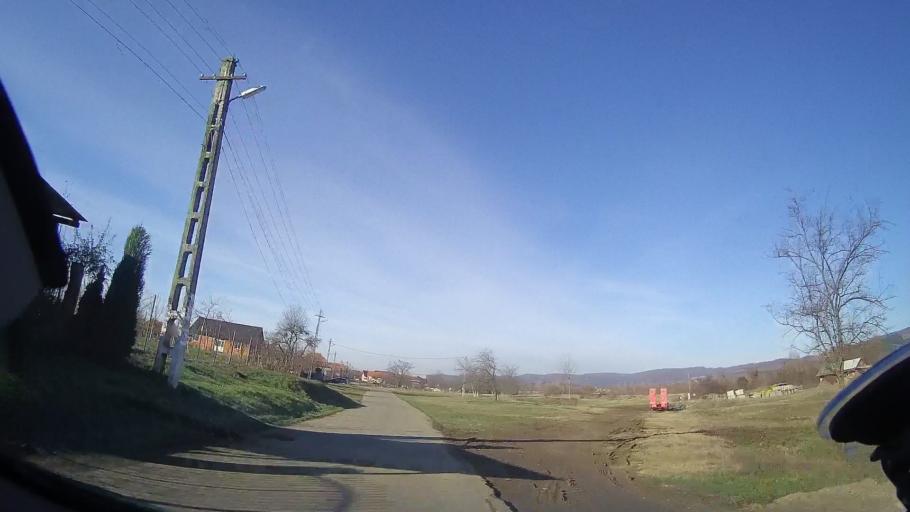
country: RO
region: Bihor
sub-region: Comuna Auseu
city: Auseu
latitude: 47.0233
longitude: 22.4929
